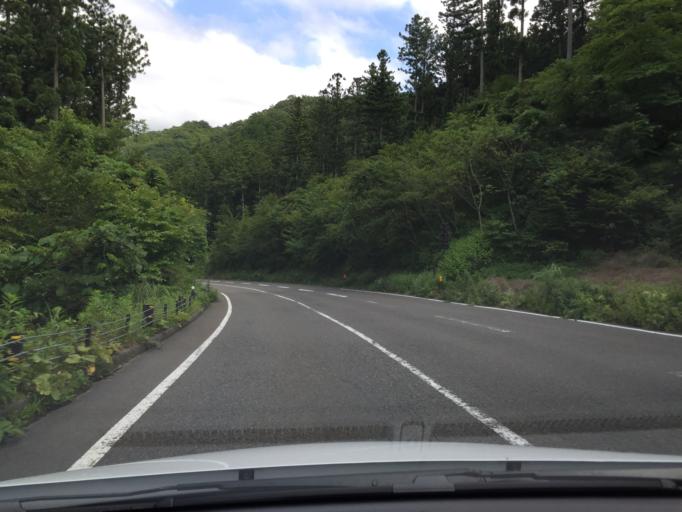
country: JP
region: Tochigi
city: Kuroiso
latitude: 37.2052
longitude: 140.1014
